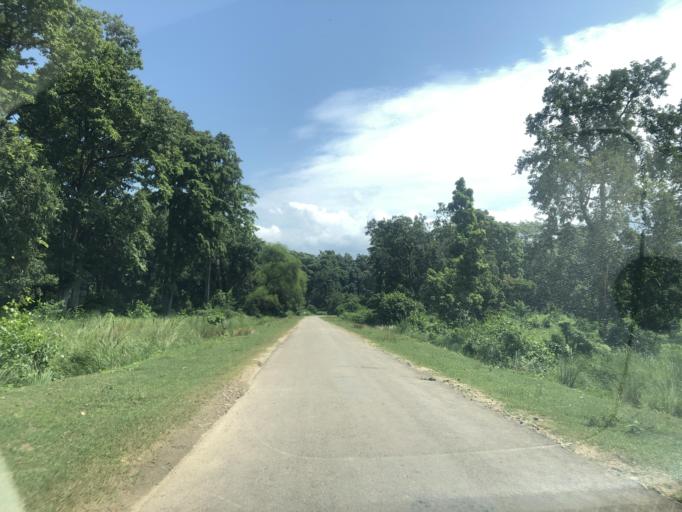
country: NP
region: Far Western
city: Tikapur
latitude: 28.5101
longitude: 81.3207
